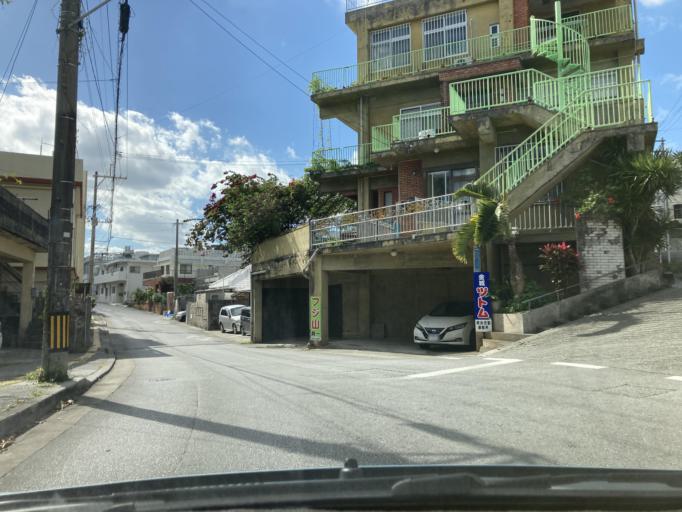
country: JP
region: Okinawa
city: Okinawa
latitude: 26.3412
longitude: 127.8019
